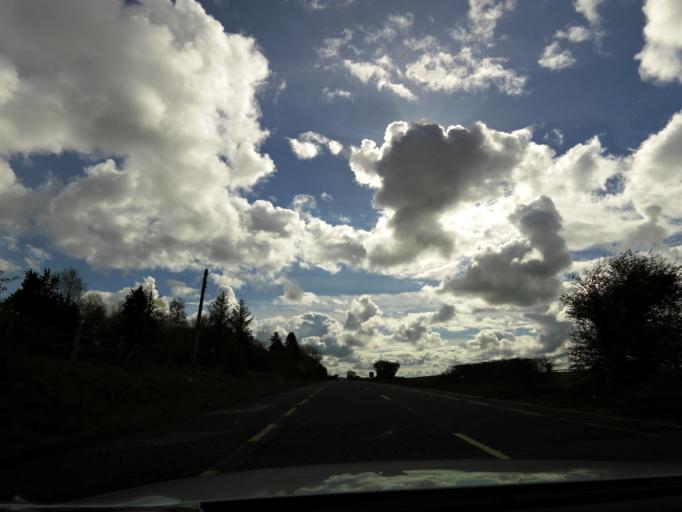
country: IE
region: Leinster
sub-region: Laois
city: Rathdowney
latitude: 52.8057
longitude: -7.4967
